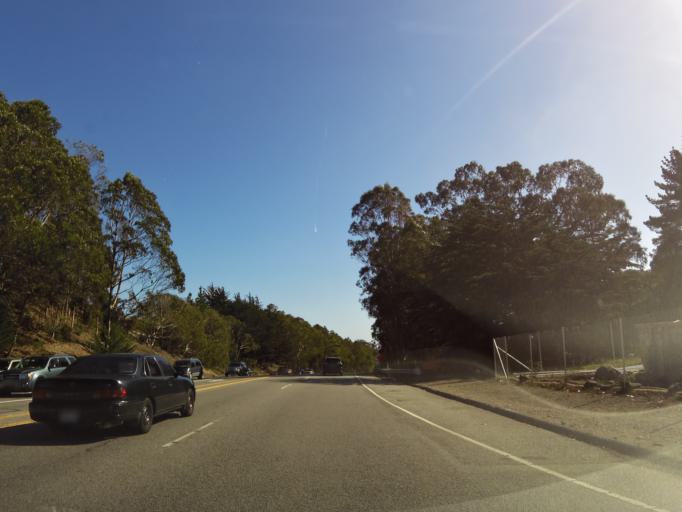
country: US
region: California
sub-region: San Mateo County
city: Pacifica
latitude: 37.6319
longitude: -122.4542
